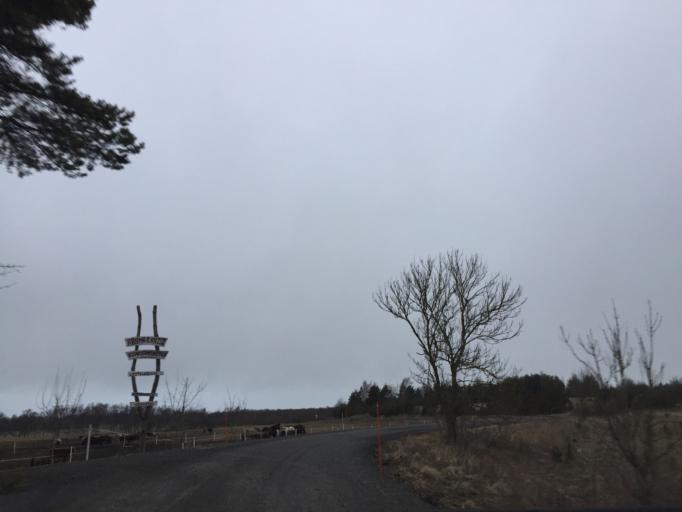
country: EE
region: Laeaene
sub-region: Haapsalu linn
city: Haapsalu
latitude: 58.6754
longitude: 23.5445
